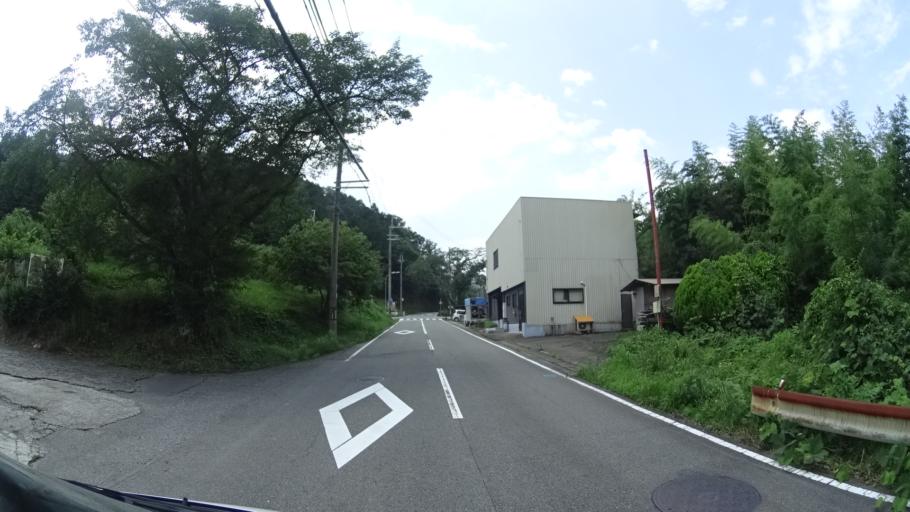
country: JP
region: Hyogo
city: Sasayama
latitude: 35.1666
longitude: 135.2687
